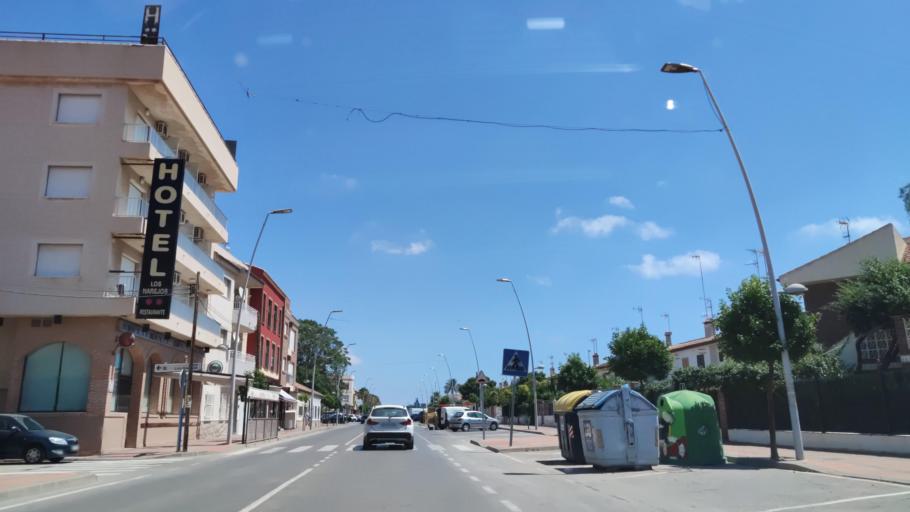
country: ES
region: Murcia
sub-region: Murcia
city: Los Alcazares
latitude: 37.7572
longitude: -0.8399
